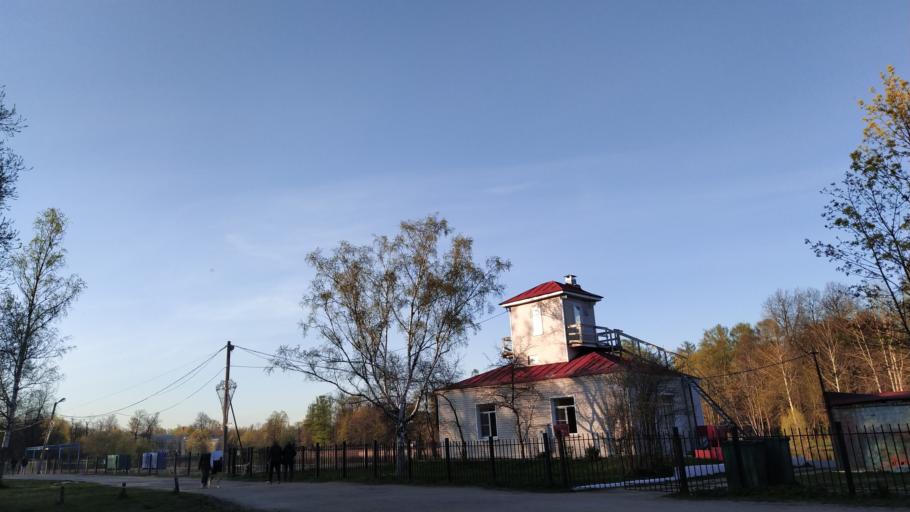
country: RU
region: St.-Petersburg
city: Pushkin
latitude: 59.7116
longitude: 30.4200
